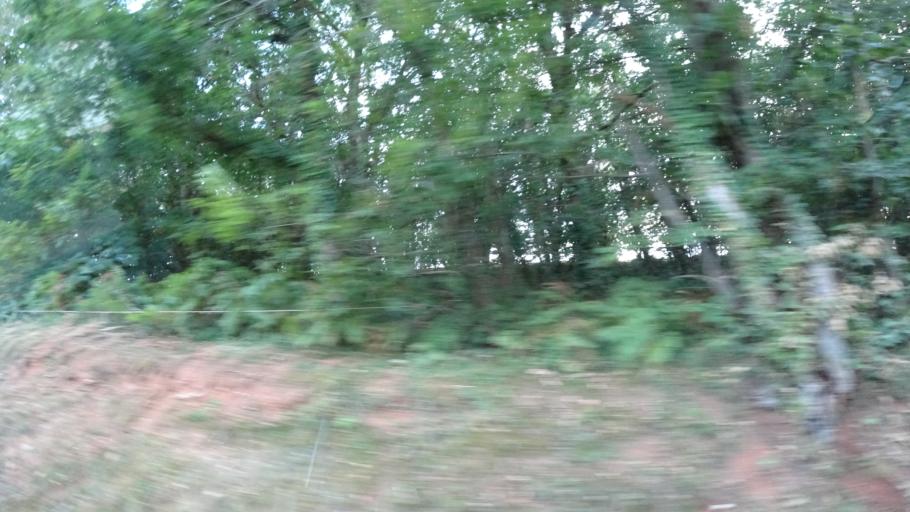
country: FR
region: Midi-Pyrenees
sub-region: Departement de l'Aveyron
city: Livinhac-le-Haut
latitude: 44.6045
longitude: 2.2594
